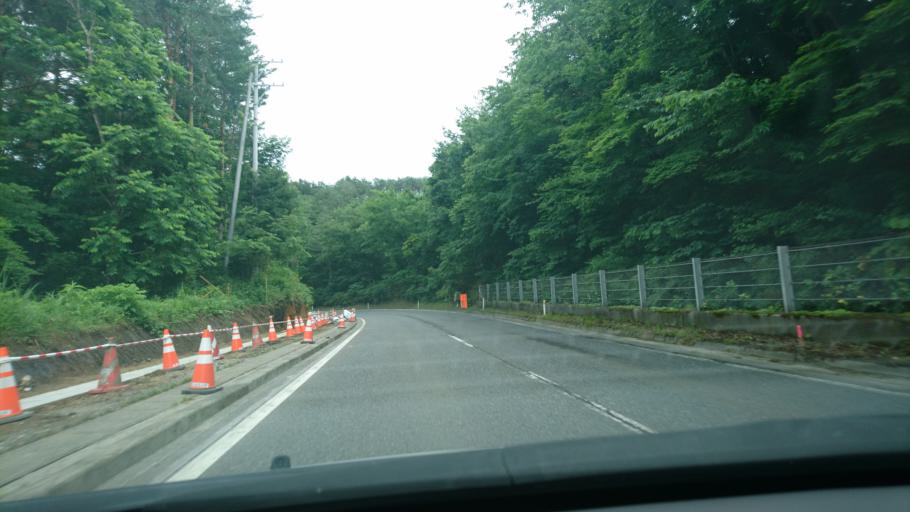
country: JP
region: Iwate
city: Miyako
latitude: 39.9552
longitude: 141.8455
